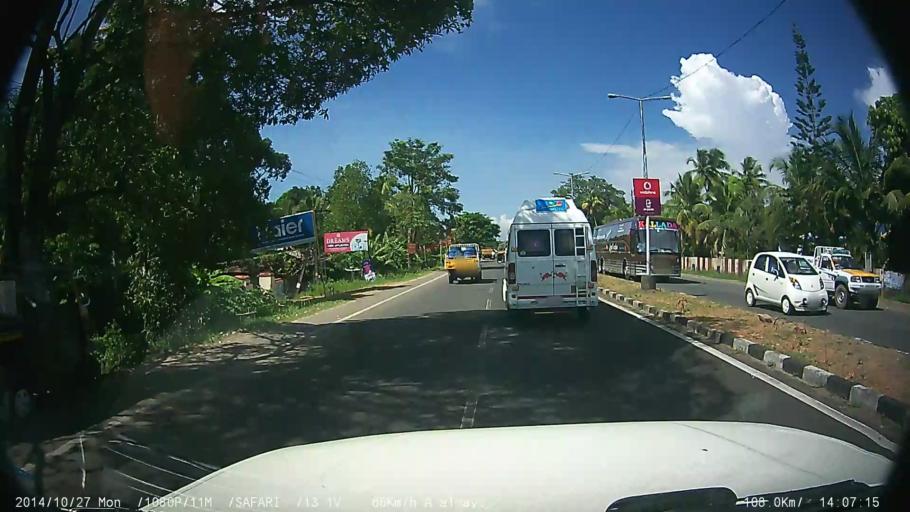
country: IN
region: Kerala
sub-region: Alappuzha
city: Kutiatodu
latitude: 9.7579
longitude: 76.3180
